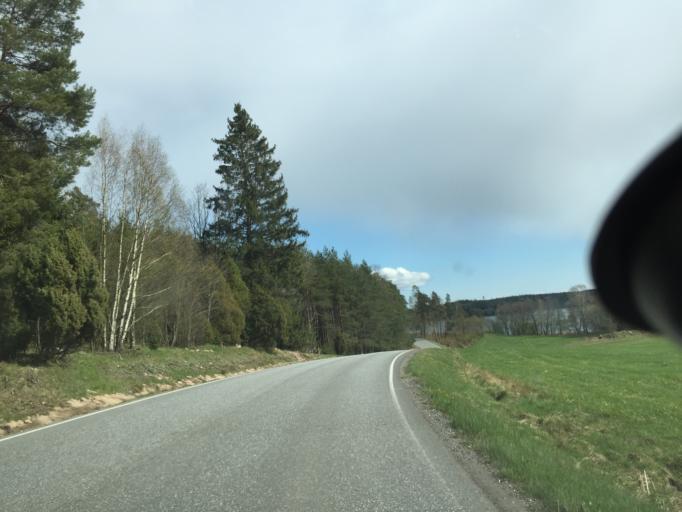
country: FI
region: Varsinais-Suomi
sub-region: Salo
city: Pernioe
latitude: 60.0335
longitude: 23.1907
